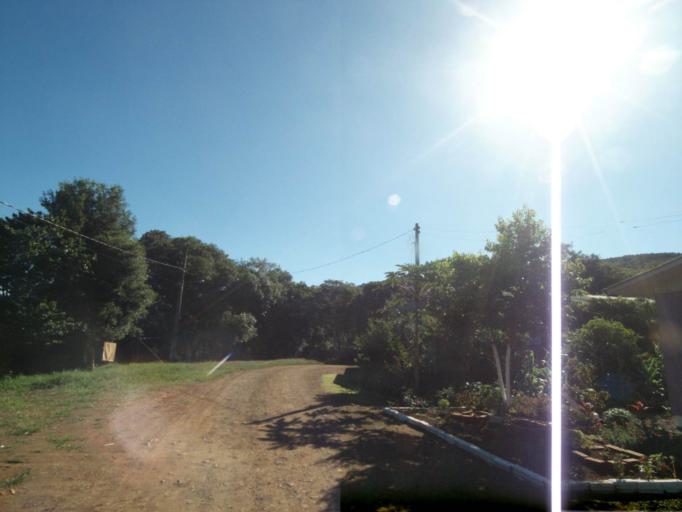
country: BR
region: Parana
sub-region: Ampere
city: Ampere
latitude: -26.1779
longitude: -53.3648
